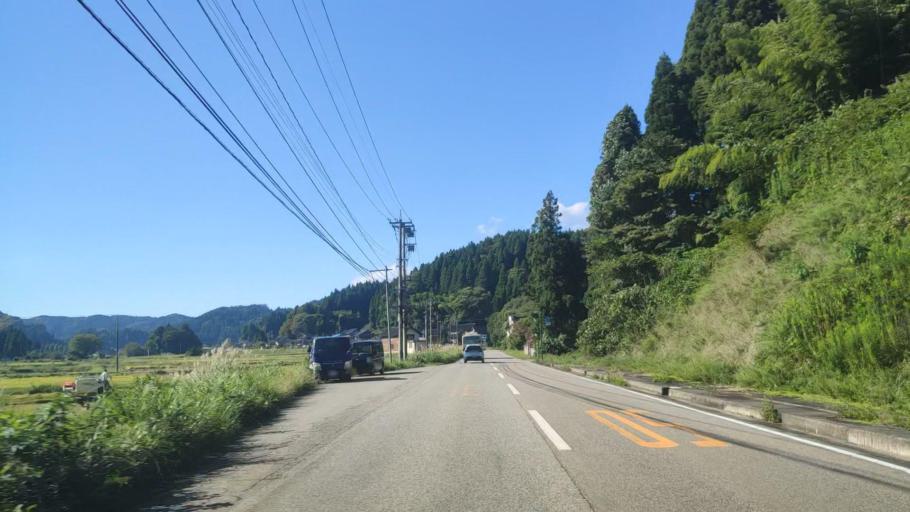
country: JP
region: Ishikawa
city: Nanao
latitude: 37.2760
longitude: 137.0535
